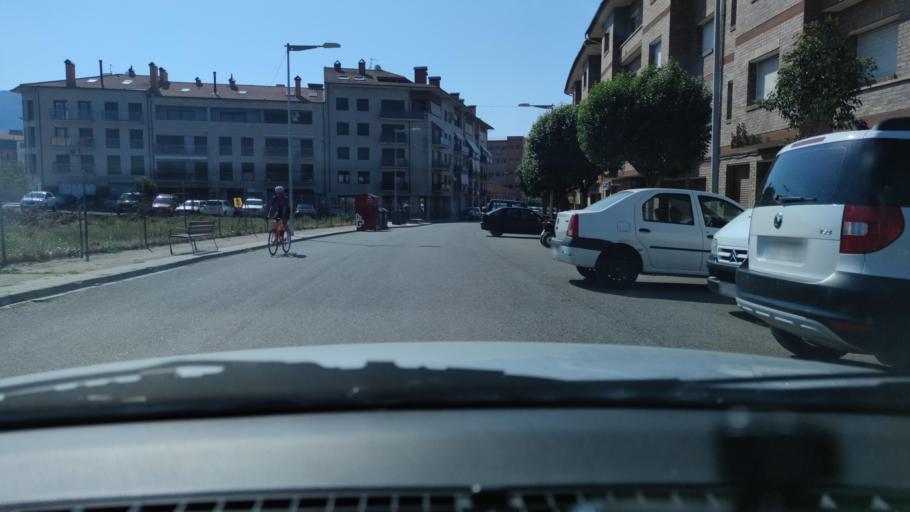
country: ES
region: Catalonia
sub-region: Provincia de Lleida
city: Senterada
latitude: 42.2514
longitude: 0.9636
